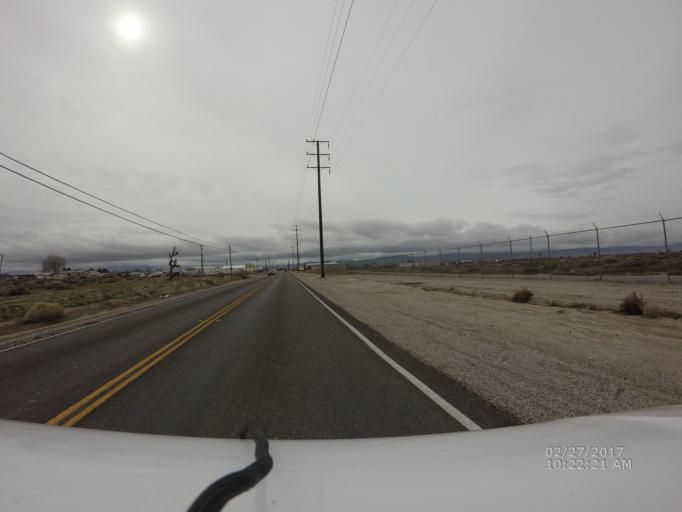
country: US
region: California
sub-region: Los Angeles County
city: Lancaster
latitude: 34.7305
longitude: -118.1308
